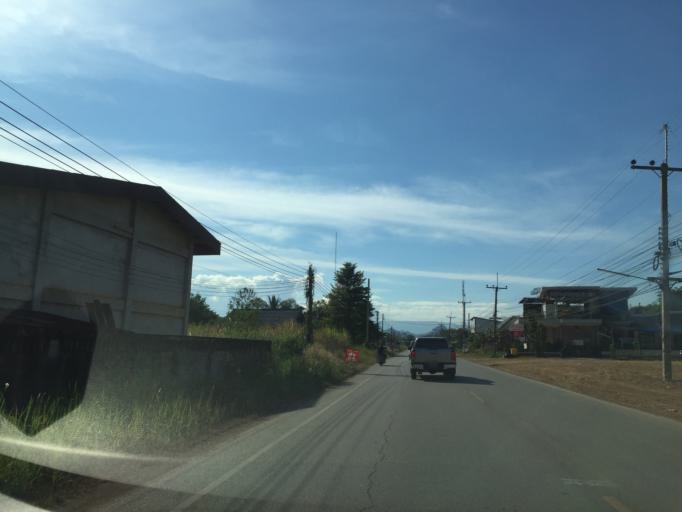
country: TH
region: Loei
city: Wang Saphung
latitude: 17.3154
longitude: 101.7584
